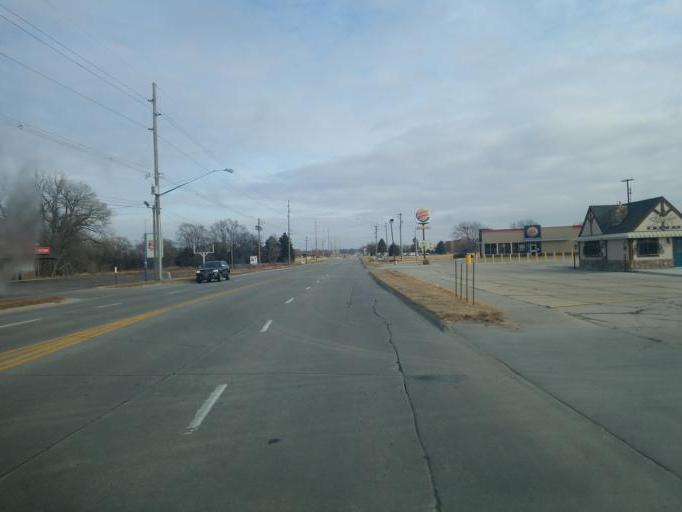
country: US
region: Nebraska
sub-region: Madison County
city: Norfolk
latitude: 42.0471
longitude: -97.4153
